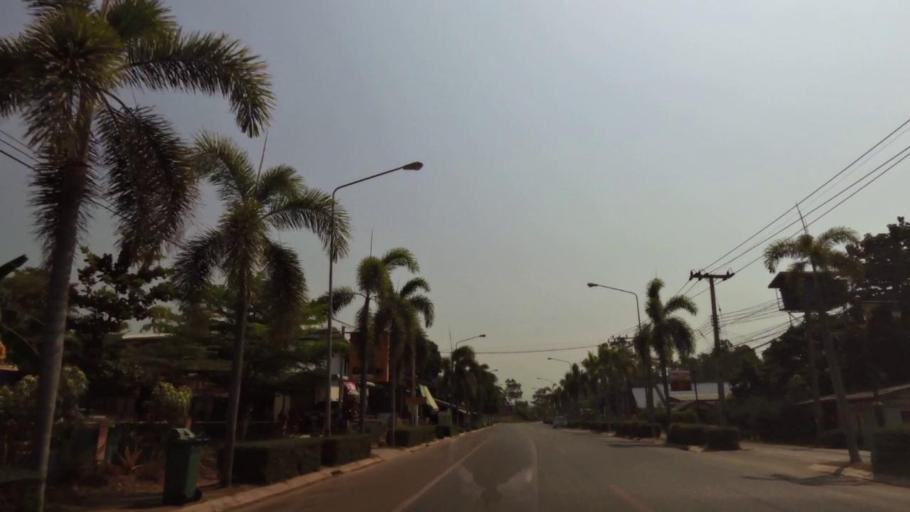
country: TH
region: Chanthaburi
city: Tha Mai
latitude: 12.5512
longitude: 101.9244
